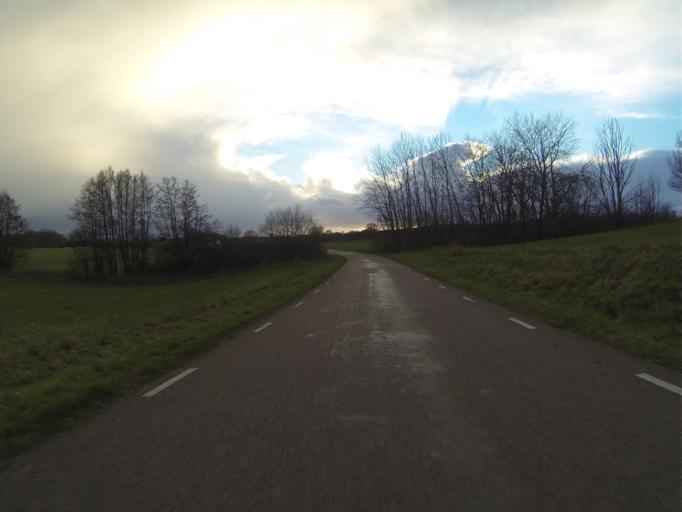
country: SE
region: Skane
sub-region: Lunds Kommun
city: Genarp
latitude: 55.5550
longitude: 13.3504
